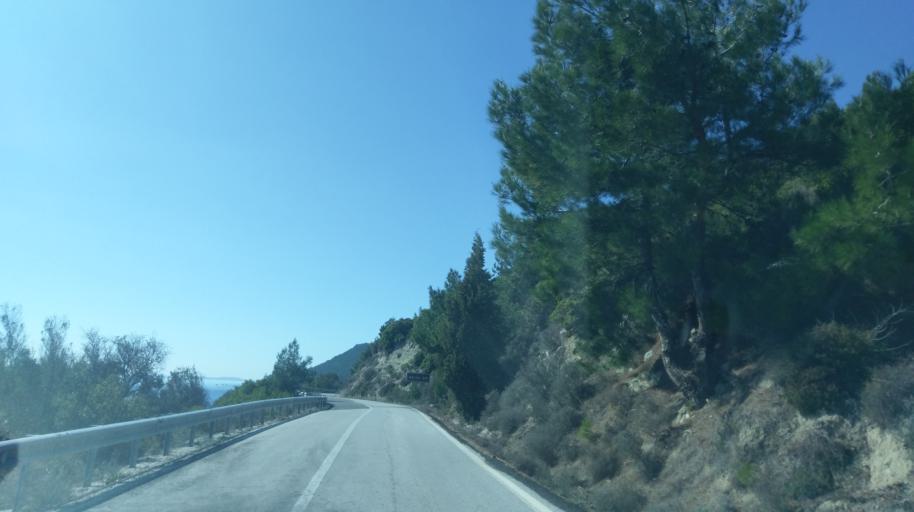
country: TR
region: Canakkale
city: Eceabat
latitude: 40.1060
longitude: 26.3263
